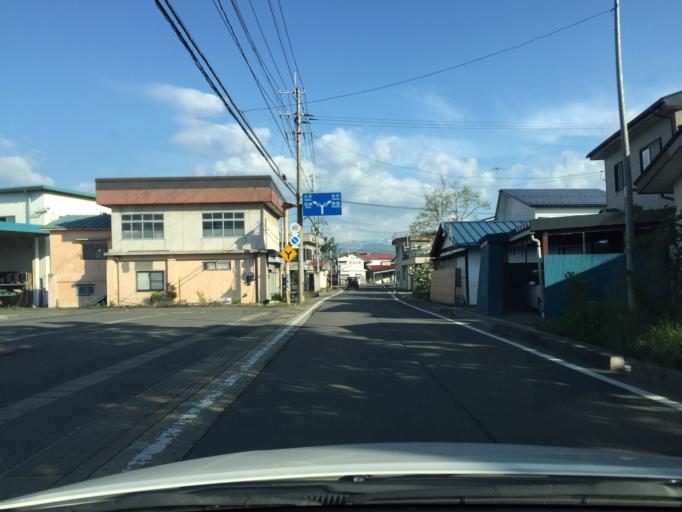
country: JP
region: Fukushima
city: Kitakata
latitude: 37.6768
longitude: 139.8706
